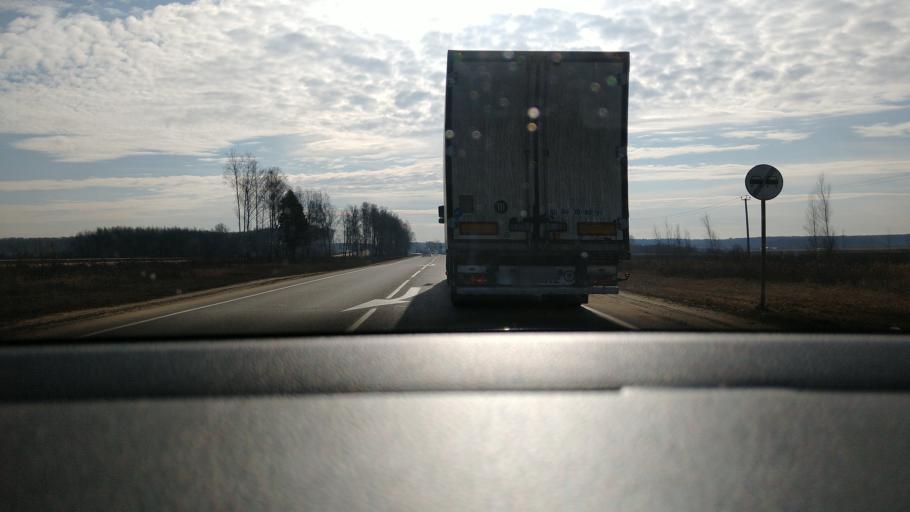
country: RU
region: Moskovskaya
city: Klimovsk
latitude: 55.3566
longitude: 37.4384
